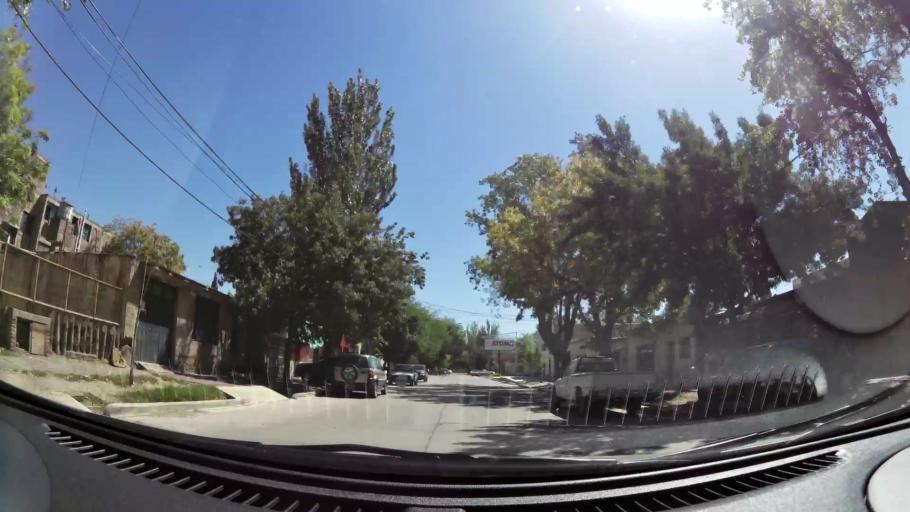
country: AR
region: Mendoza
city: Mendoza
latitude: -32.8763
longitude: -68.8187
